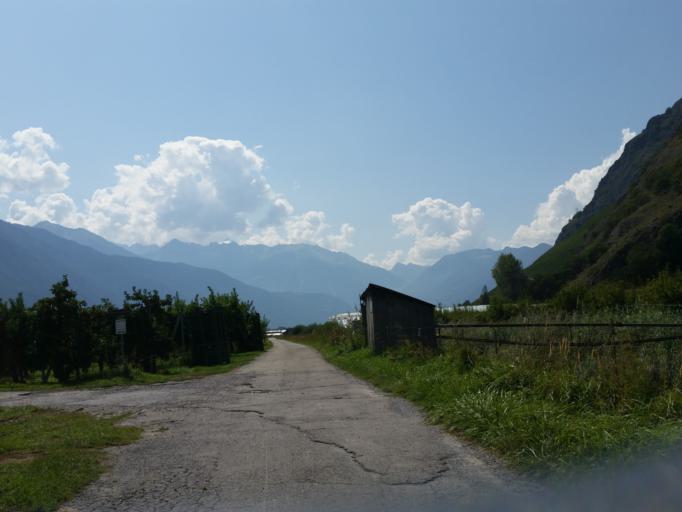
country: CH
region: Valais
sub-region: Martigny District
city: Saillon
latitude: 46.1660
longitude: 7.1697
